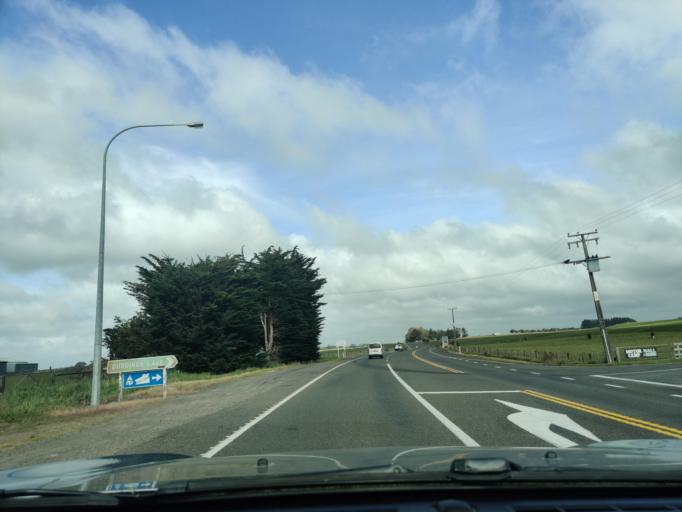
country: NZ
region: Manawatu-Wanganui
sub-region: Rangitikei District
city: Bulls
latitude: -40.0942
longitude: 175.2846
